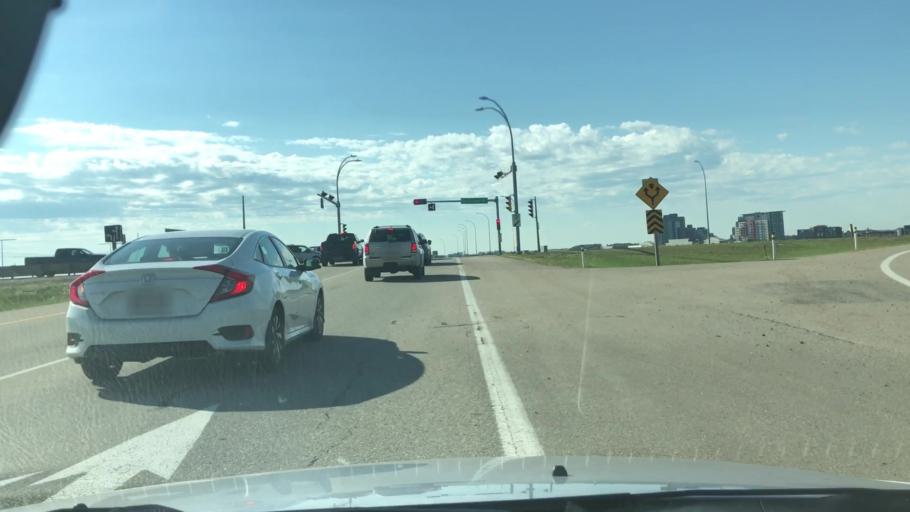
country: CA
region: Alberta
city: Devon
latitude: 53.4444
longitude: -113.6020
